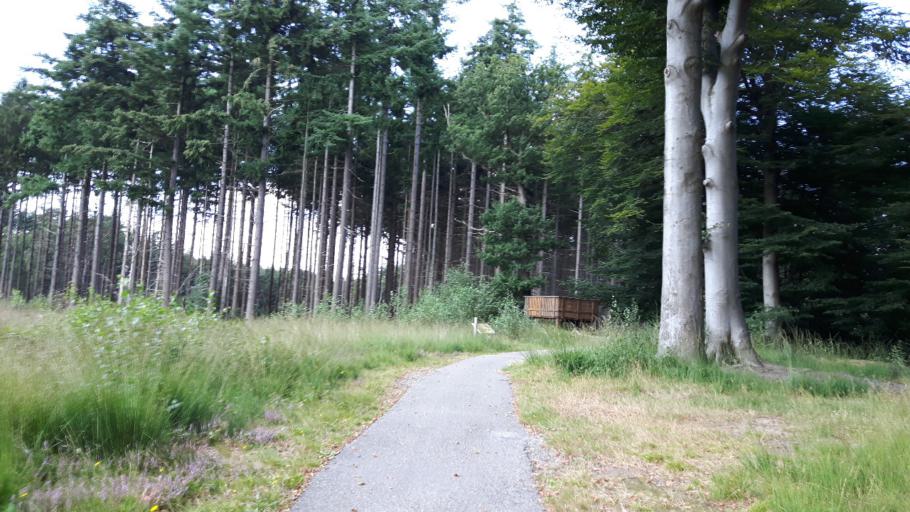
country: NL
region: Friesland
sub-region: Gemeente Smallingerland
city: Drachtstercompagnie
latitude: 53.0775
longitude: 6.2434
